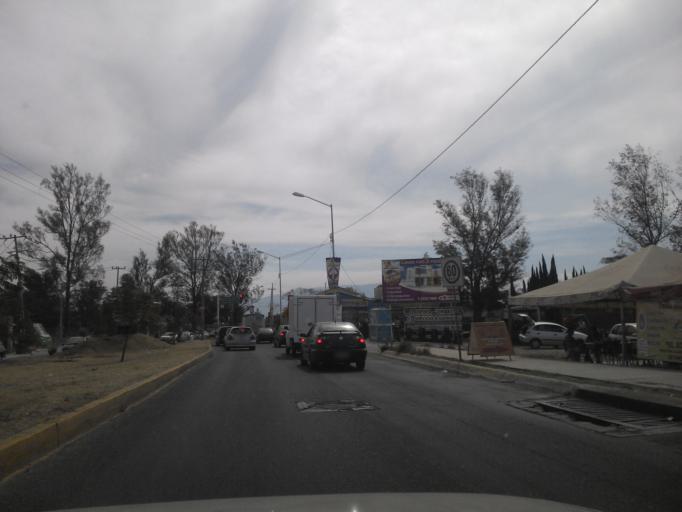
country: MX
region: Jalisco
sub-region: San Pedro Tlaquepaque
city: Paseo del Prado
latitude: 20.5638
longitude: -103.3924
